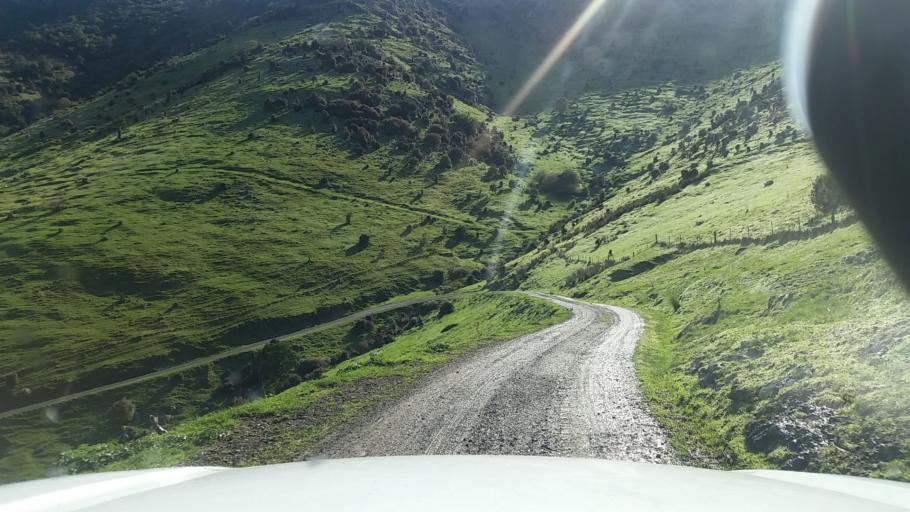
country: NZ
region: Canterbury
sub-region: Christchurch City
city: Christchurch
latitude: -43.6657
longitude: 172.8735
